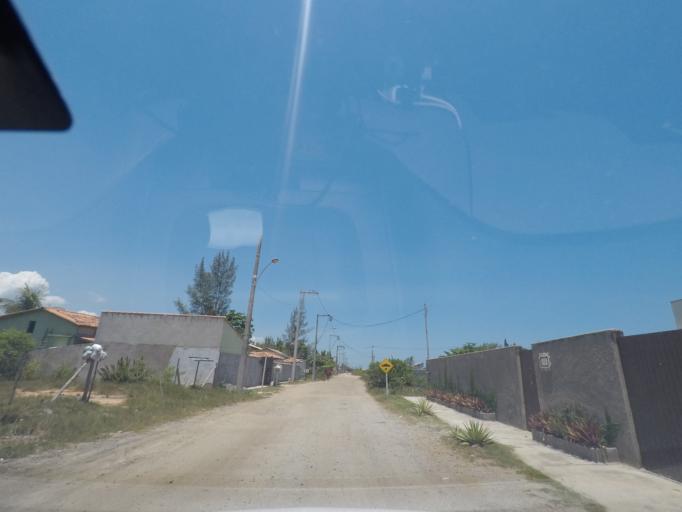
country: BR
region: Rio de Janeiro
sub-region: Niteroi
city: Niteroi
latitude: -22.9681
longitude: -42.9830
